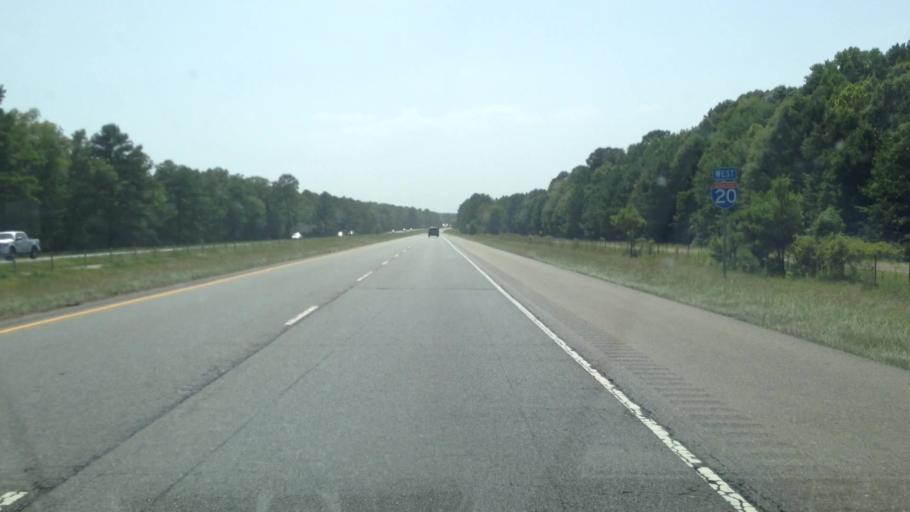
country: US
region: Louisiana
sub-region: Bossier Parish
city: Haughton
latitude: 32.5782
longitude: -93.4411
